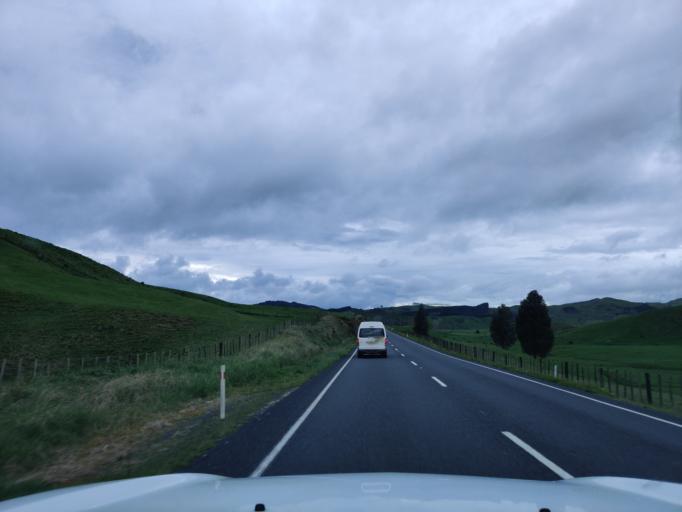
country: NZ
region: Waikato
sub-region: Otorohanga District
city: Otorohanga
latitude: -38.4631
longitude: 175.1679
